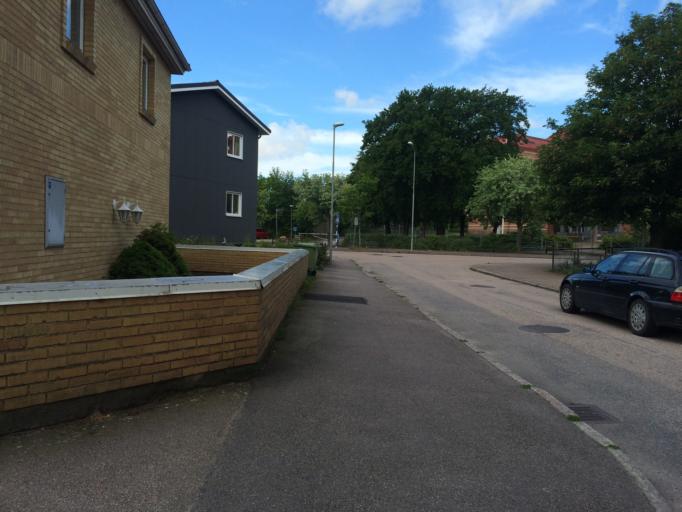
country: SE
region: Halland
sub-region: Halmstads Kommun
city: Halmstad
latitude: 56.6721
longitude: 12.8461
